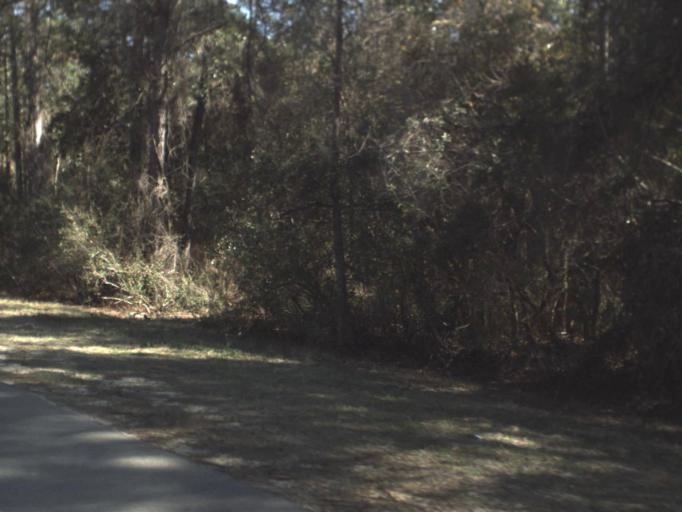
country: US
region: Florida
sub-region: Bay County
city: Youngstown
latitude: 30.4363
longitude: -85.4856
